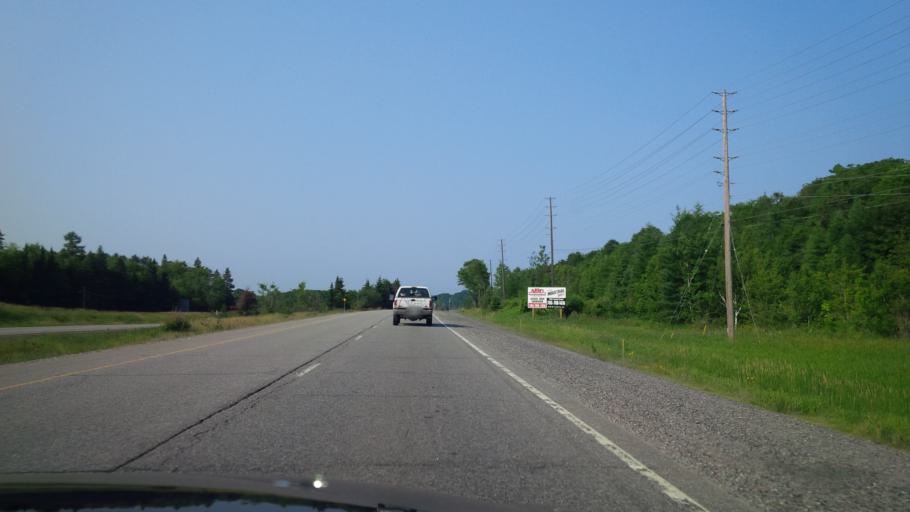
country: CA
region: Ontario
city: Huntsville
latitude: 45.2745
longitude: -79.2823
